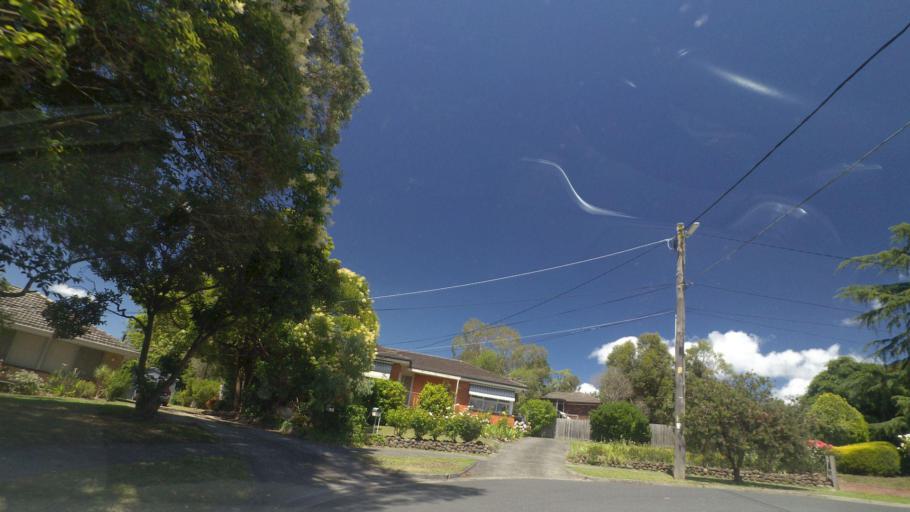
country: AU
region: Victoria
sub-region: Yarra Ranges
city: Kilsyth
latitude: -37.7836
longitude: 145.3209
